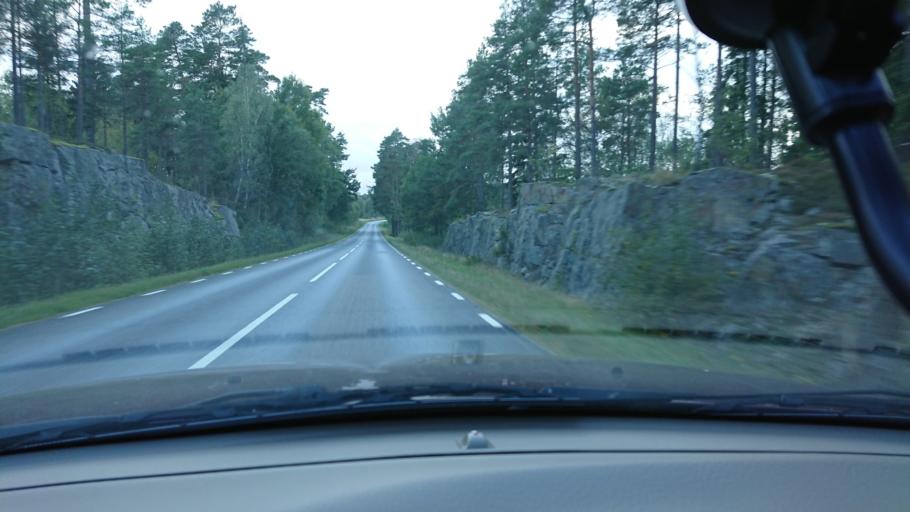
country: SE
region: Kronoberg
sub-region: Vaxjo Kommun
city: Rottne
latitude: 57.0679
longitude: 14.7314
